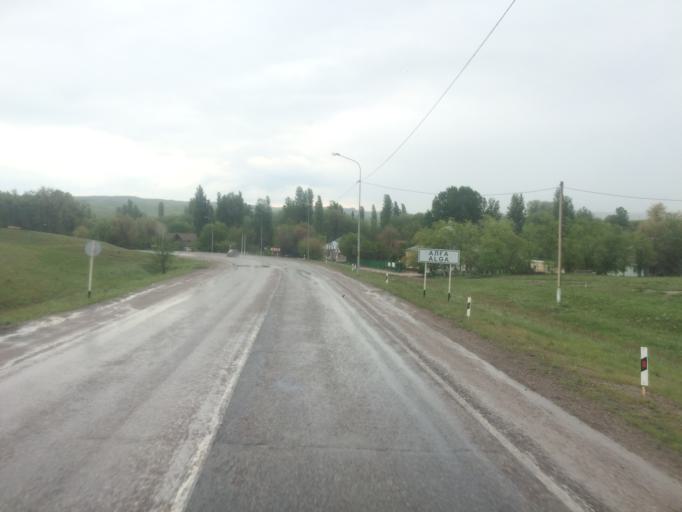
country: KZ
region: Zhambyl
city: Georgiyevka
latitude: 43.2314
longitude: 74.7601
